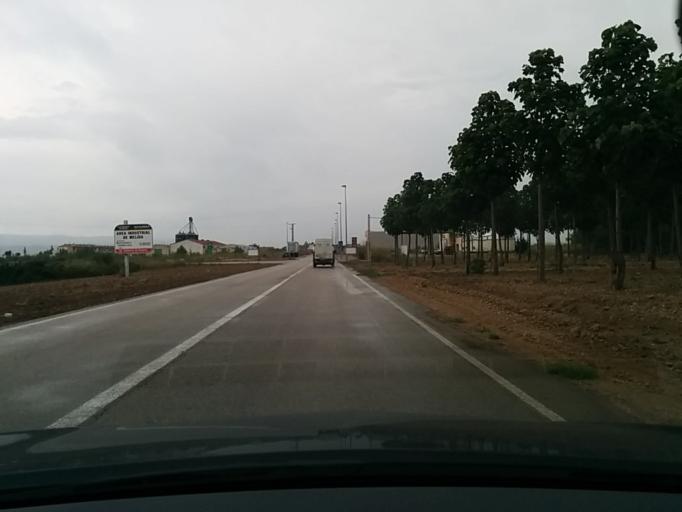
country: ES
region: Navarre
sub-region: Provincia de Navarra
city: Melida
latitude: 42.3547
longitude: -1.5595
